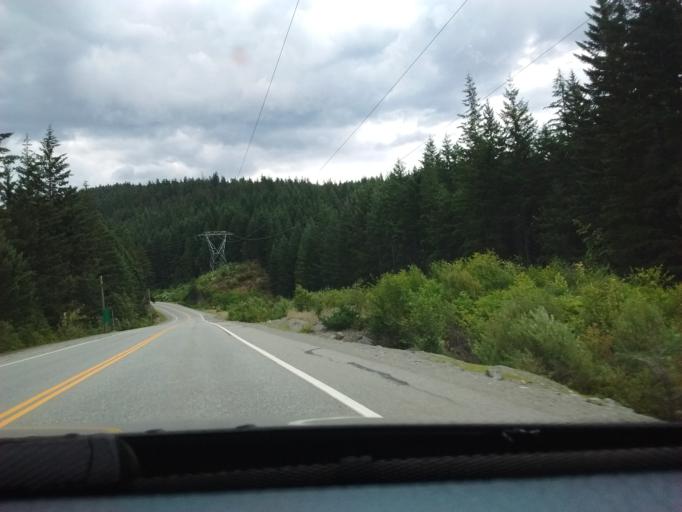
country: CA
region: British Columbia
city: Pemberton
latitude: 50.2982
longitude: -122.8167
